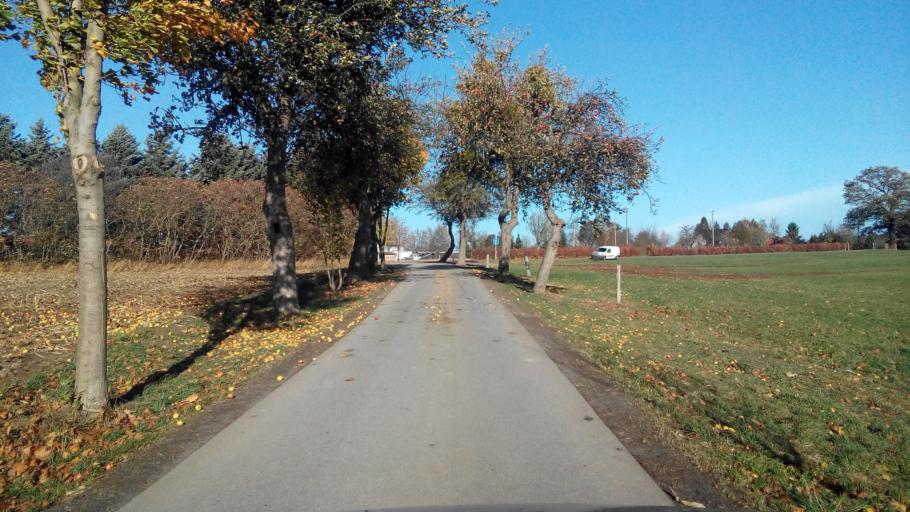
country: DE
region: Saxony
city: Bernstadt
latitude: 51.0633
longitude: 14.7944
